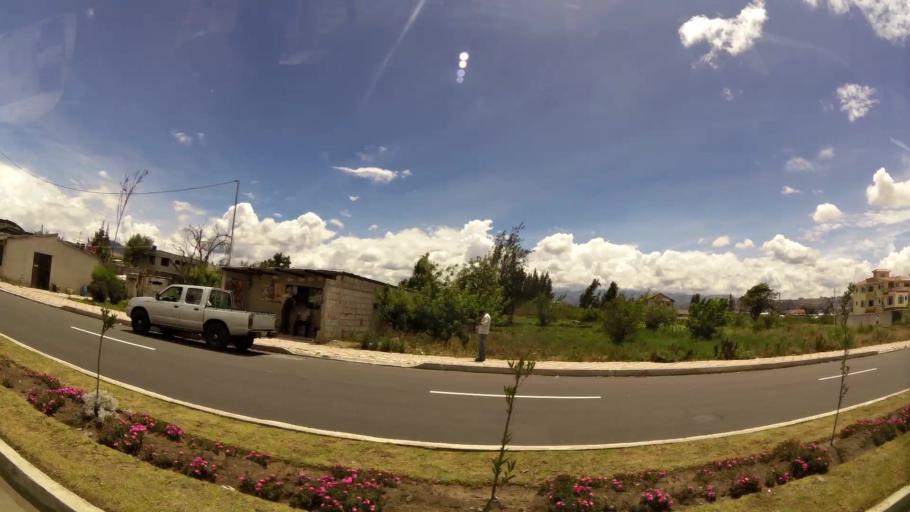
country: EC
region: Tungurahua
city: Ambato
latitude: -1.2647
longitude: -78.6040
